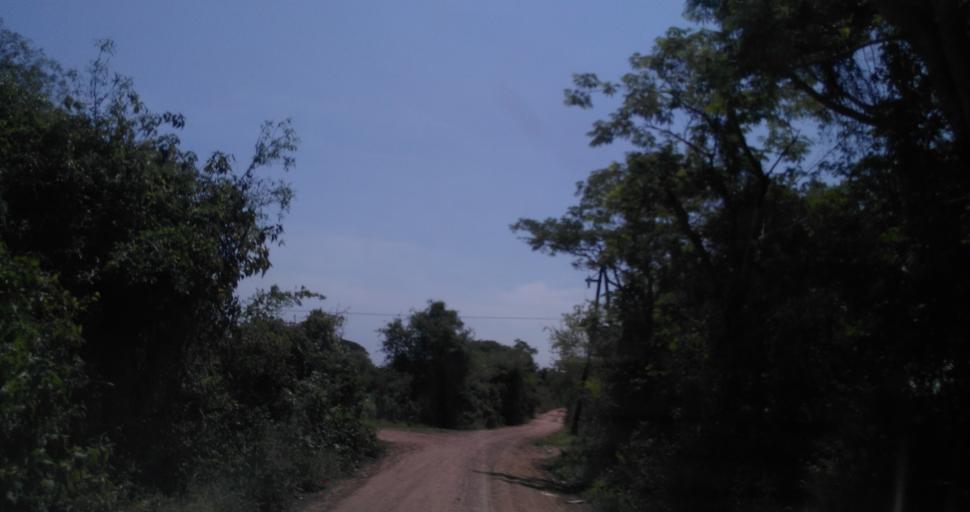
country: AR
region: Chaco
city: Fontana
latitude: -27.4132
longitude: -59.0125
